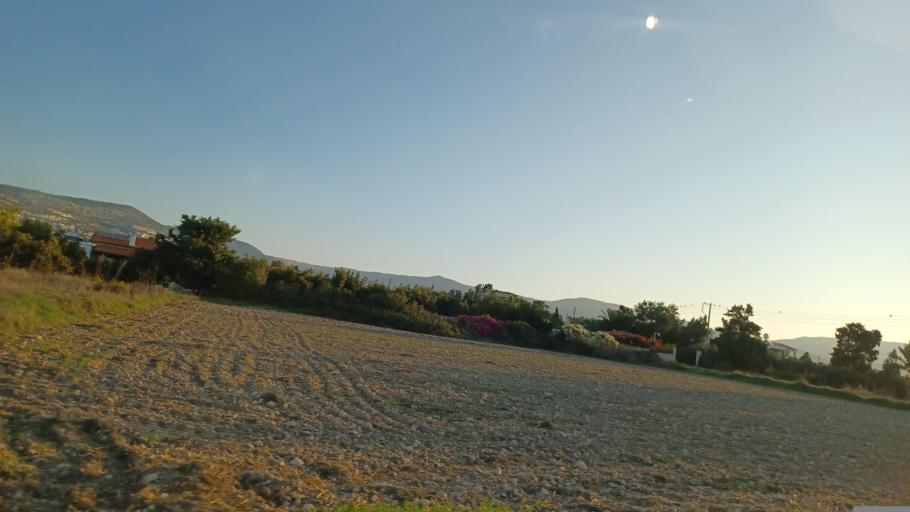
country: CY
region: Pafos
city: Pegeia
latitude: 34.8668
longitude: 32.3577
